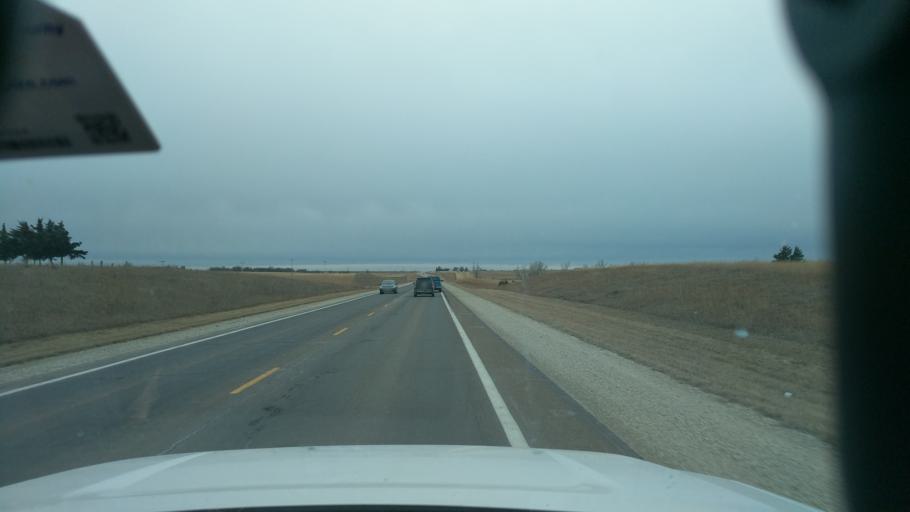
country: US
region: Kansas
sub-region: Dickinson County
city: Herington
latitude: 38.6155
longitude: -96.9487
